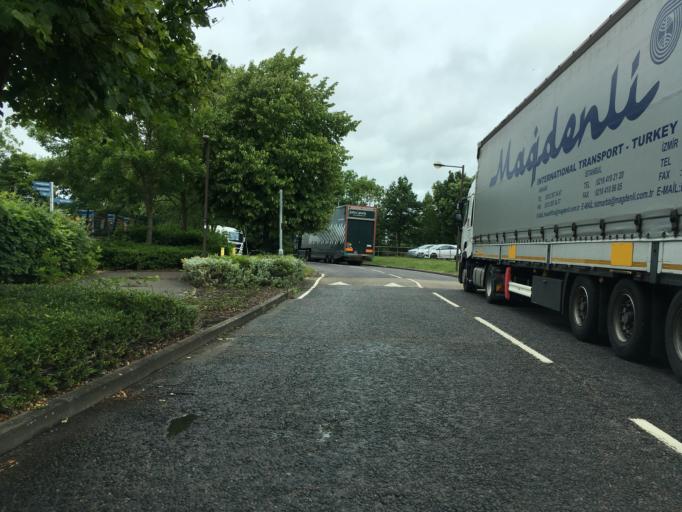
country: GB
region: England
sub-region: Milton Keynes
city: Broughton
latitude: 52.0366
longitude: -0.6860
